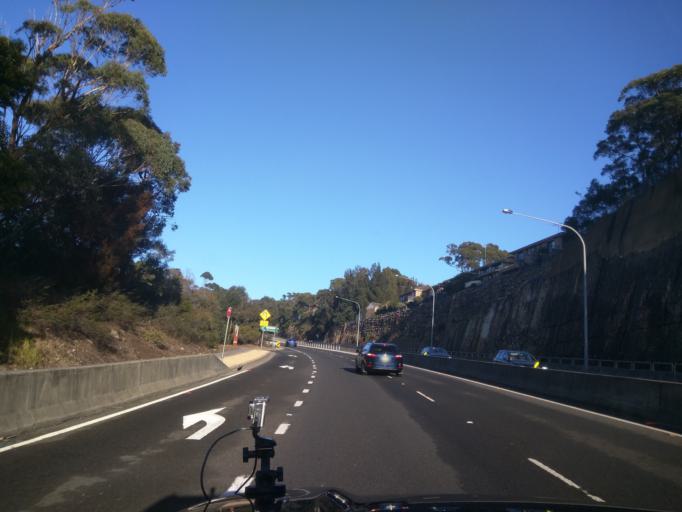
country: AU
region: New South Wales
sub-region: Sutherland Shire
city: Bonnet Bay
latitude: -34.0195
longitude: 151.0457
